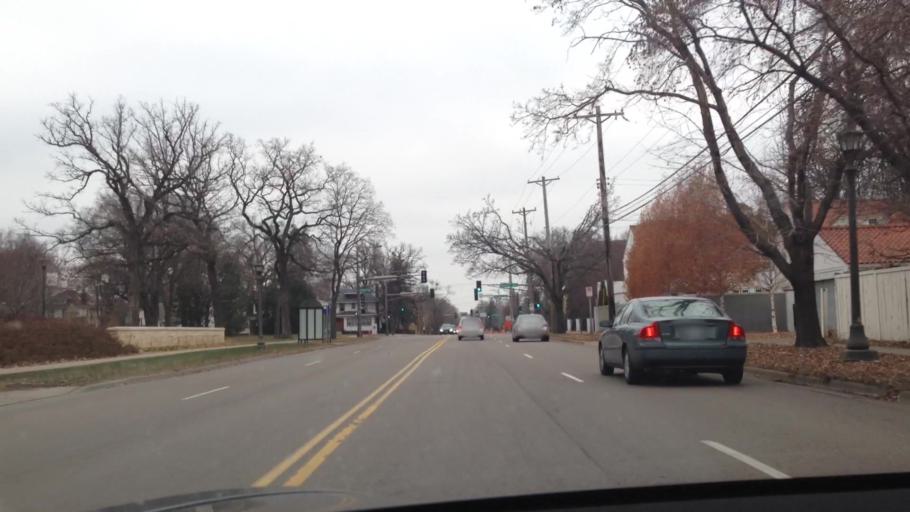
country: US
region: Minnesota
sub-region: Ramsey County
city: Falcon Heights
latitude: 44.9427
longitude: -93.1925
